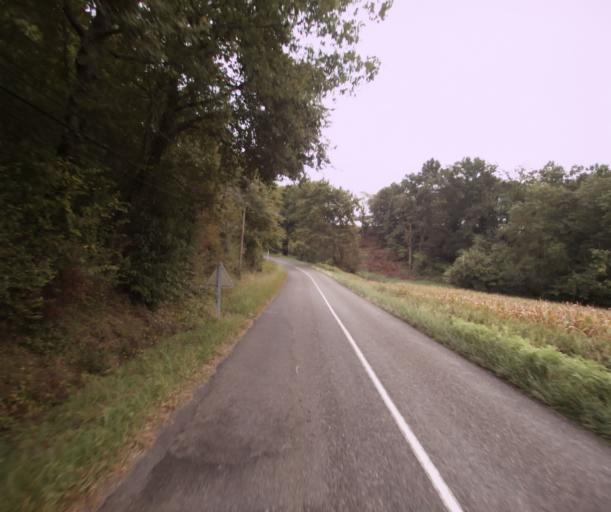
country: FR
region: Midi-Pyrenees
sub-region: Departement du Gers
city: Cazaubon
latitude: 43.8668
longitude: -0.0976
